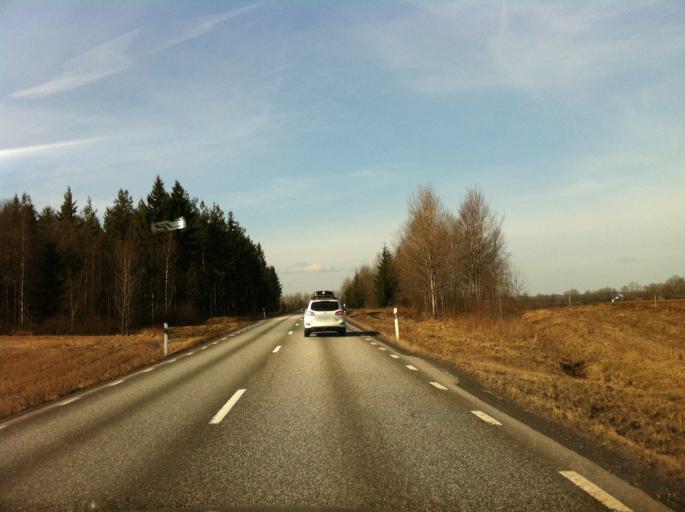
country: SE
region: Joenkoeping
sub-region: Habo Kommun
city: Habo
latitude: 57.8566
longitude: 14.0145
